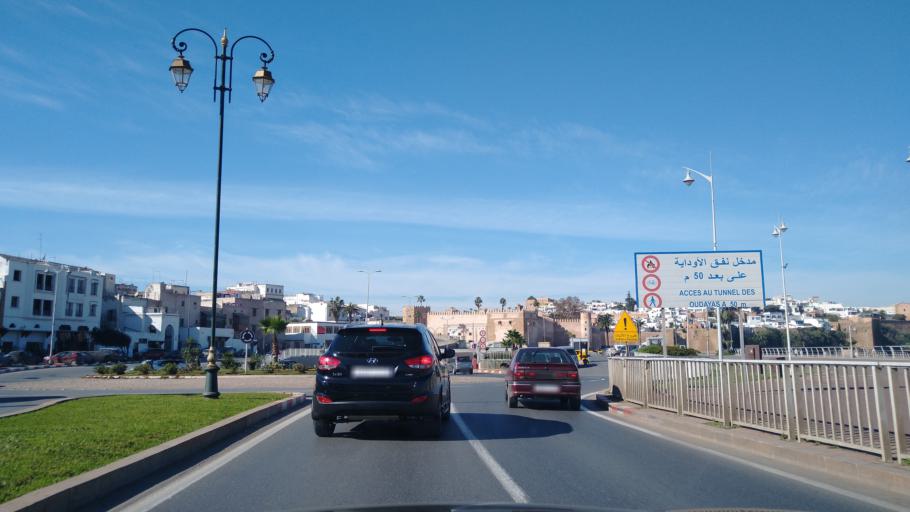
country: MA
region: Rabat-Sale-Zemmour-Zaer
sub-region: Rabat
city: Rabat
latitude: 34.0281
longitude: -6.8323
